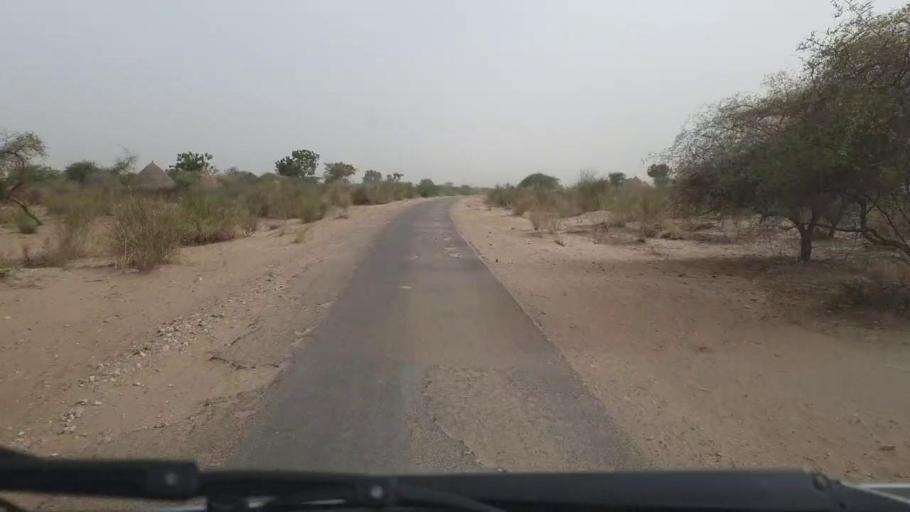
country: PK
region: Sindh
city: Islamkot
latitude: 25.0730
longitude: 70.5643
